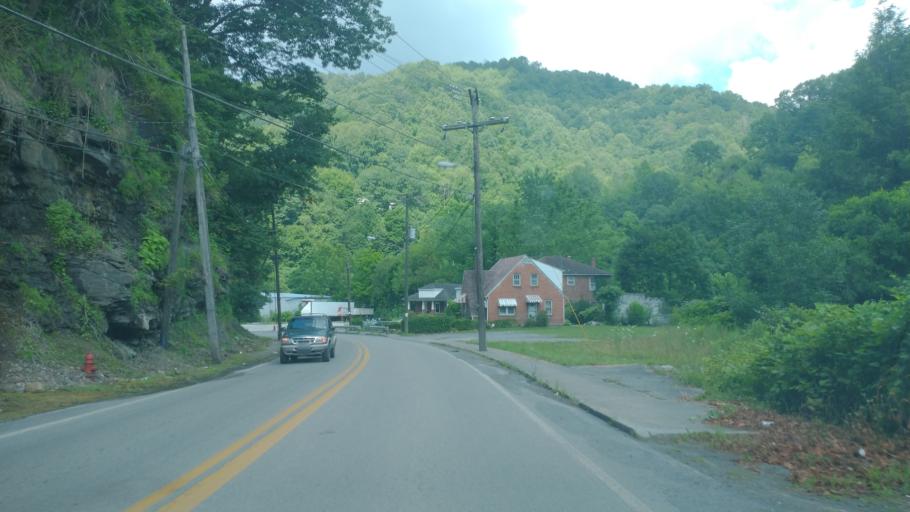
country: US
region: West Virginia
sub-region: McDowell County
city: Welch
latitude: 37.4162
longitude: -81.4489
